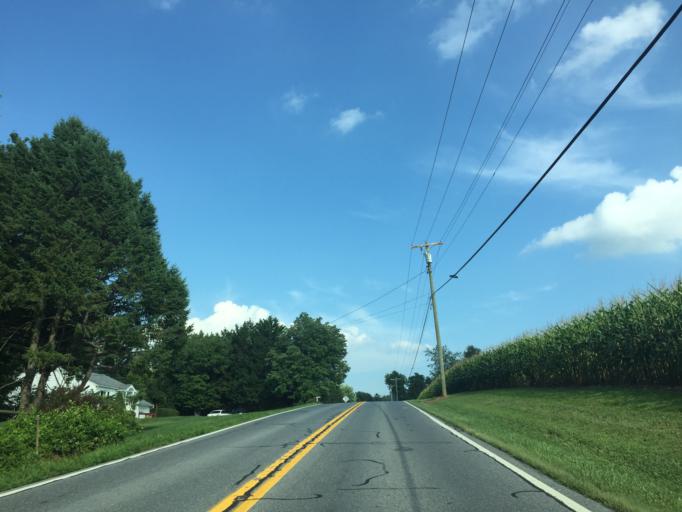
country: US
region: Maryland
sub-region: Carroll County
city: Hampstead
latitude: 39.5933
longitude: -76.7488
